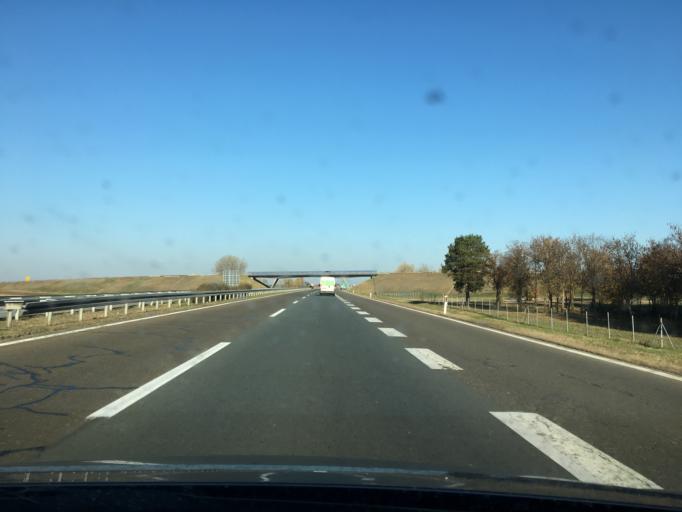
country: RS
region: Autonomna Pokrajina Vojvodina
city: Nova Pazova
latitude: 44.9847
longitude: 20.2170
